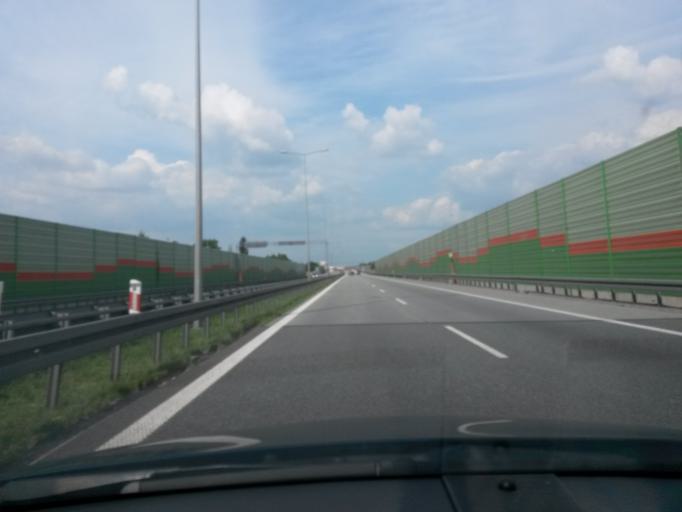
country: PL
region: Lodz Voivodeship
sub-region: Powiat rawski
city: Rawa Mazowiecka
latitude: 51.7507
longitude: 20.2479
